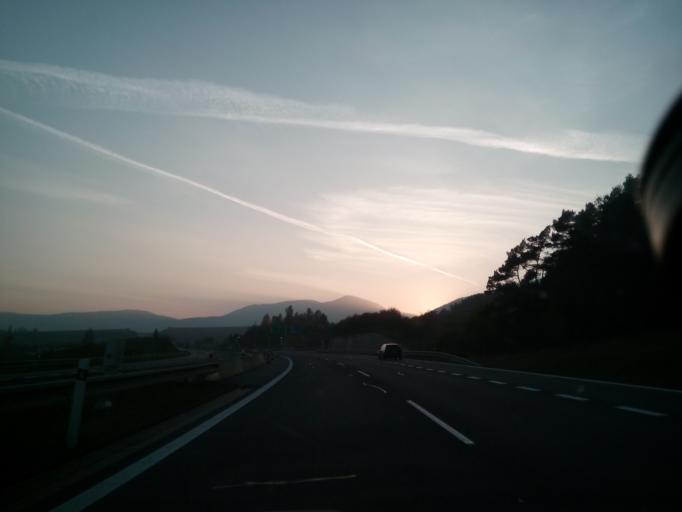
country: SK
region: Kosicky
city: Krompachy
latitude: 49.0139
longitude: 20.9447
